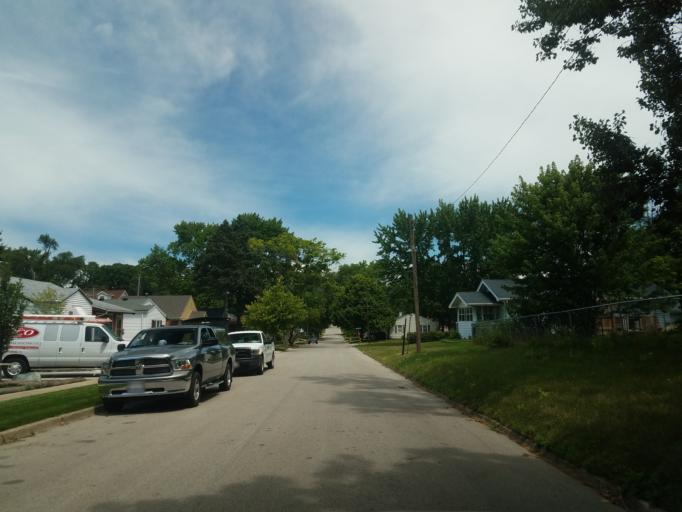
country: US
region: Illinois
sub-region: McLean County
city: Bloomington
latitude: 40.4680
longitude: -88.9837
